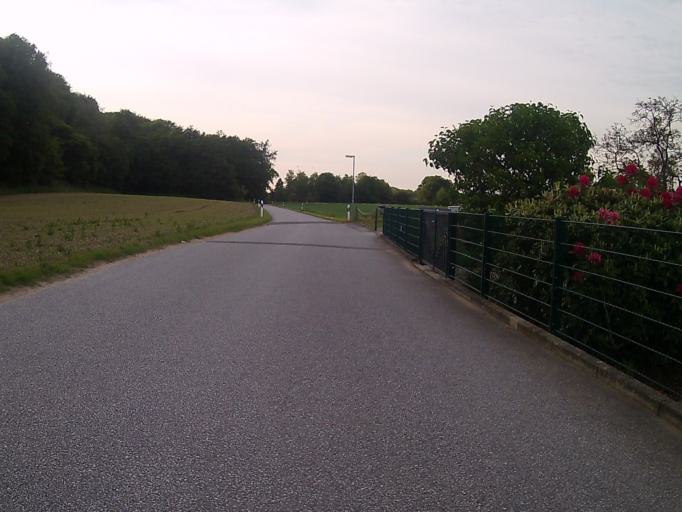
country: DE
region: North Rhine-Westphalia
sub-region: Regierungsbezirk Dusseldorf
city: Rheurdt
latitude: 51.4049
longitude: 6.5260
